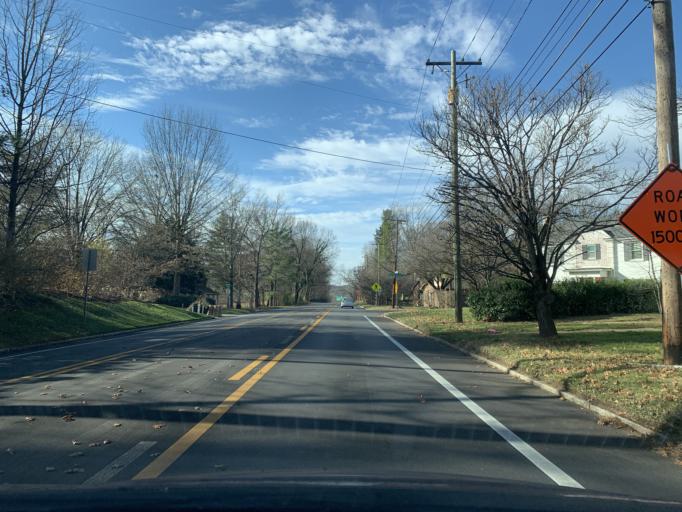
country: US
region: Kentucky
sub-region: Jefferson County
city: Saint Matthews
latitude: 38.2452
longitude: -85.6916
